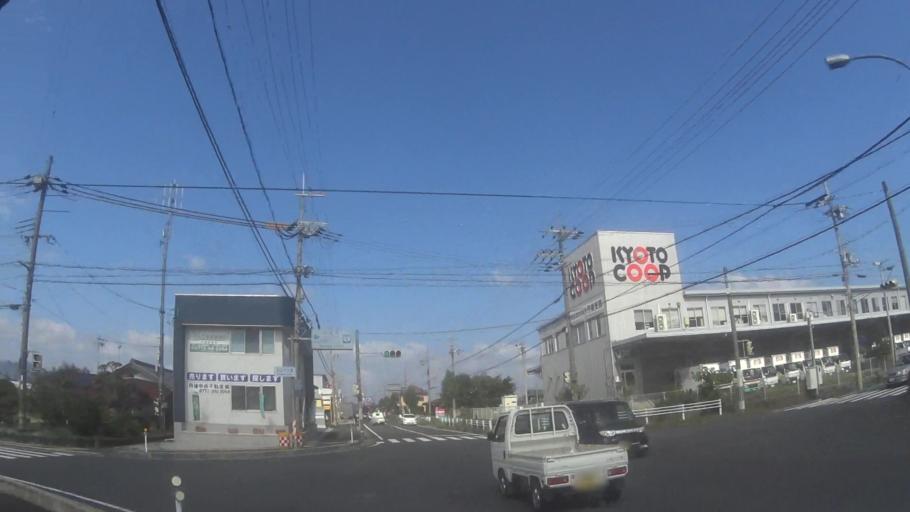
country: JP
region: Kyoto
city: Miyazu
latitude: 35.5987
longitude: 135.0880
